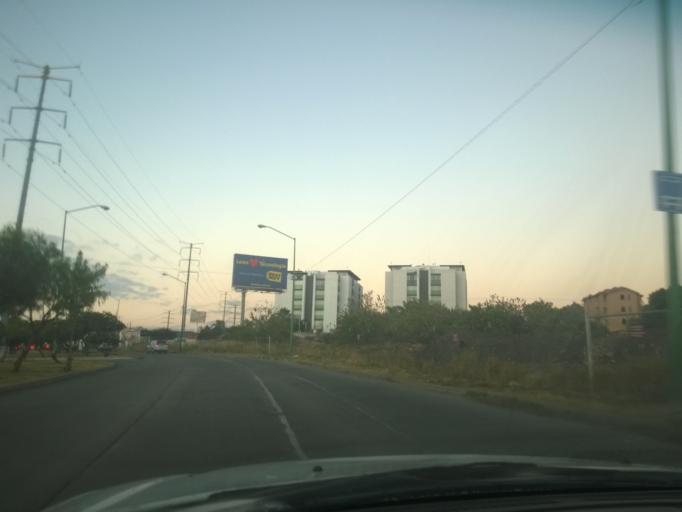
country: MX
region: Guanajuato
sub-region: Leon
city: La Ermita
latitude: 21.1487
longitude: -101.7076
